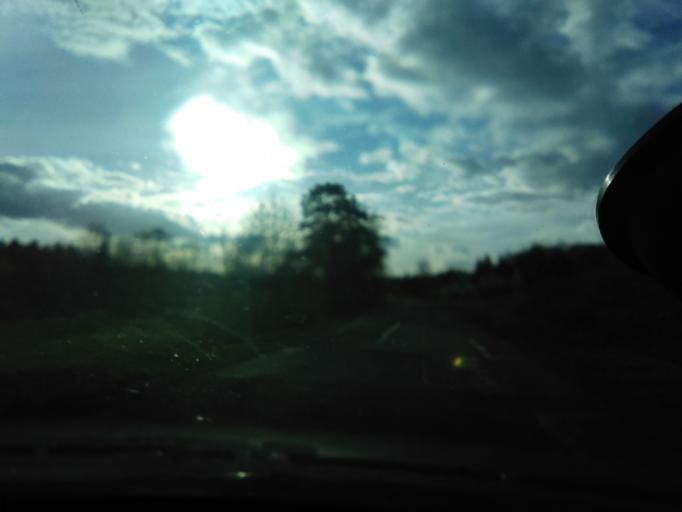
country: PL
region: Subcarpathian Voivodeship
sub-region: Powiat ropczycko-sedziszowski
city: Wielopole Skrzynskie
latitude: 49.9331
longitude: 21.5626
